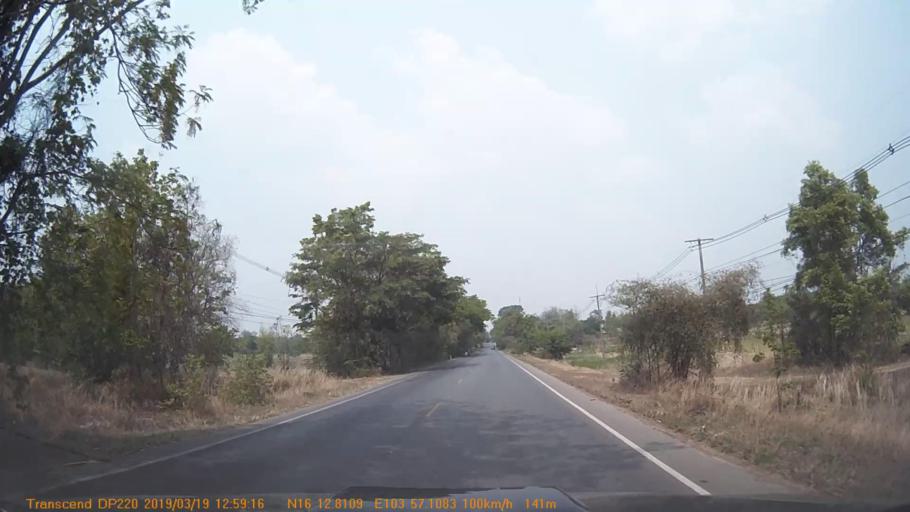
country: TH
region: Roi Et
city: Waeng
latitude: 16.2140
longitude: 103.9519
